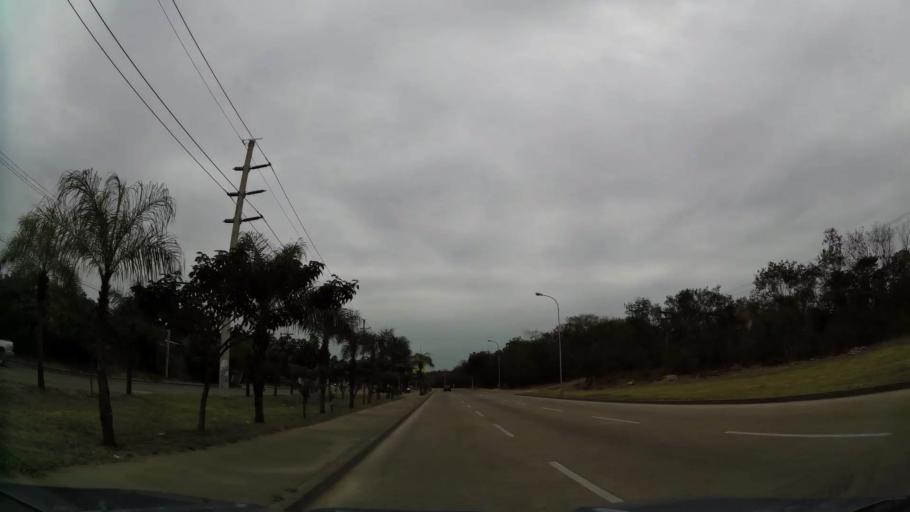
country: BO
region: Santa Cruz
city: Santa Cruz de la Sierra
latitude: -17.7750
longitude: -63.2148
